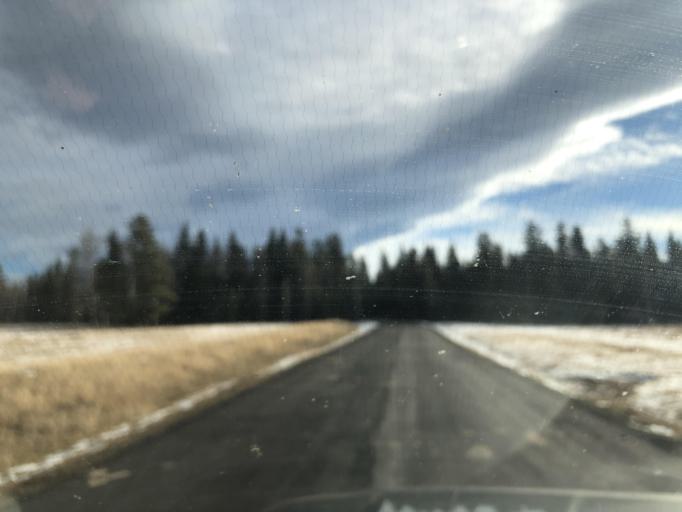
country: CA
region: Alberta
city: Cochrane
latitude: 51.0443
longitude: -114.8670
